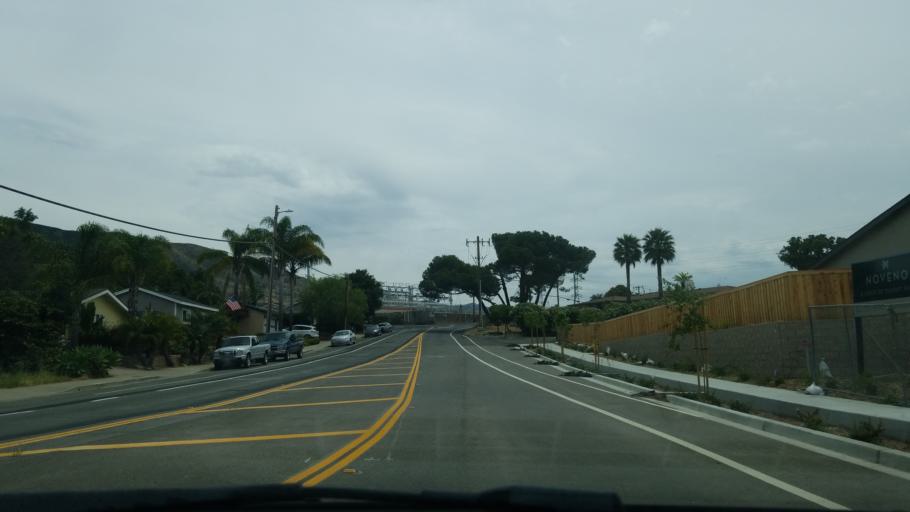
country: US
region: California
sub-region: San Luis Obispo County
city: San Luis Obispo
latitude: 35.2614
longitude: -120.6373
